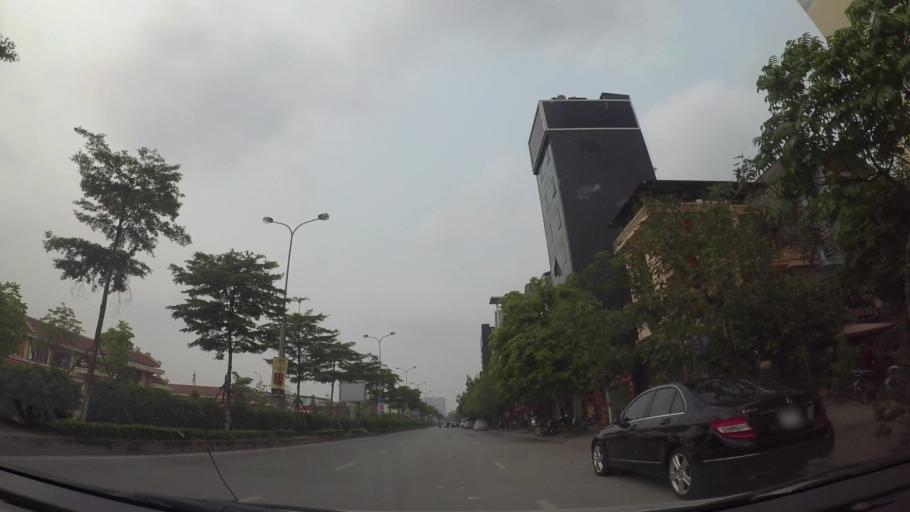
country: VN
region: Ha Noi
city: Cau Dien
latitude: 21.0404
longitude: 105.7730
